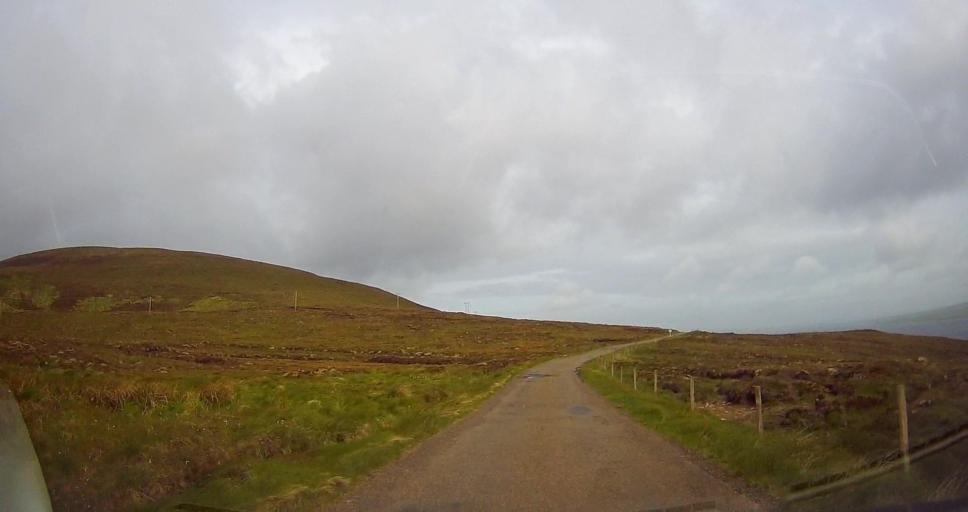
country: GB
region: Scotland
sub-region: Orkney Islands
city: Stromness
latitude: 58.8813
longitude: -3.2481
